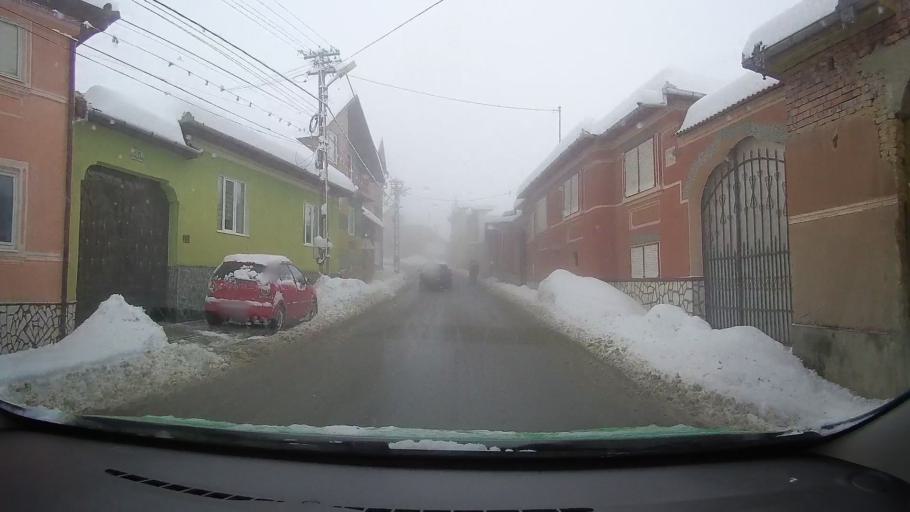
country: RO
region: Sibiu
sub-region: Comuna Jina
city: Jina
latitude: 45.7839
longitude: 23.6812
